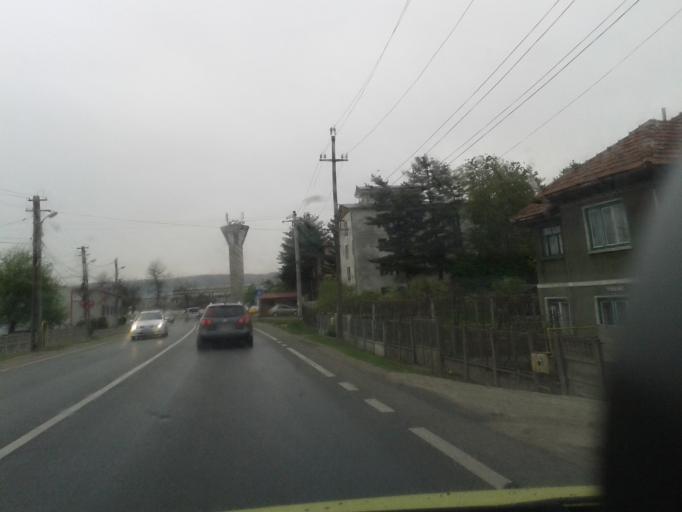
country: RO
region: Hunedoara
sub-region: Oras Simeria
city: Simeria
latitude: 45.8400
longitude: 23.0195
